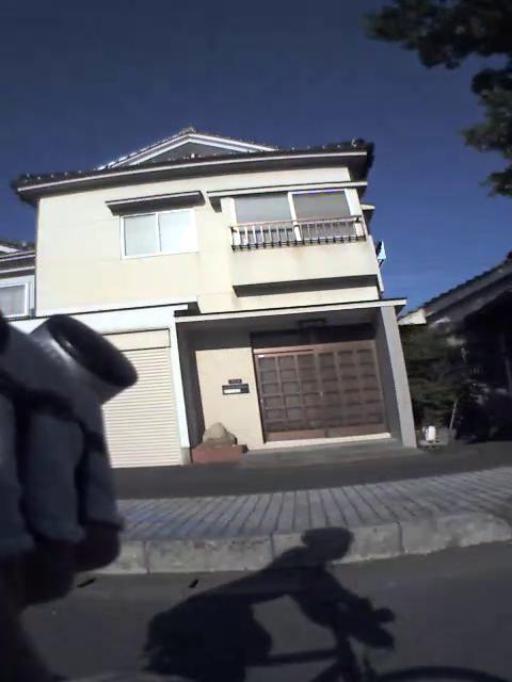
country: JP
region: Yamaguchi
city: Nagato
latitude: 34.3917
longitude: 131.2003
